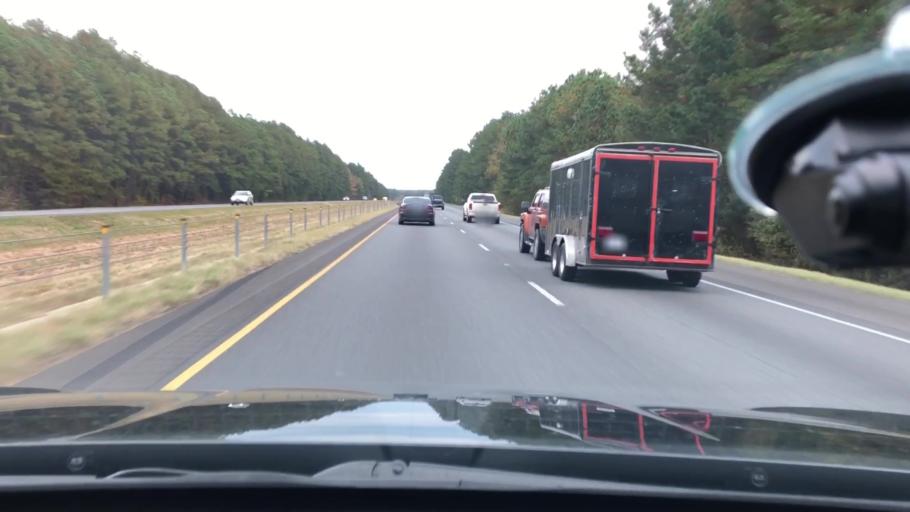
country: US
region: Arkansas
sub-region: Clark County
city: Arkadelphia
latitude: 34.2070
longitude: -93.0409
